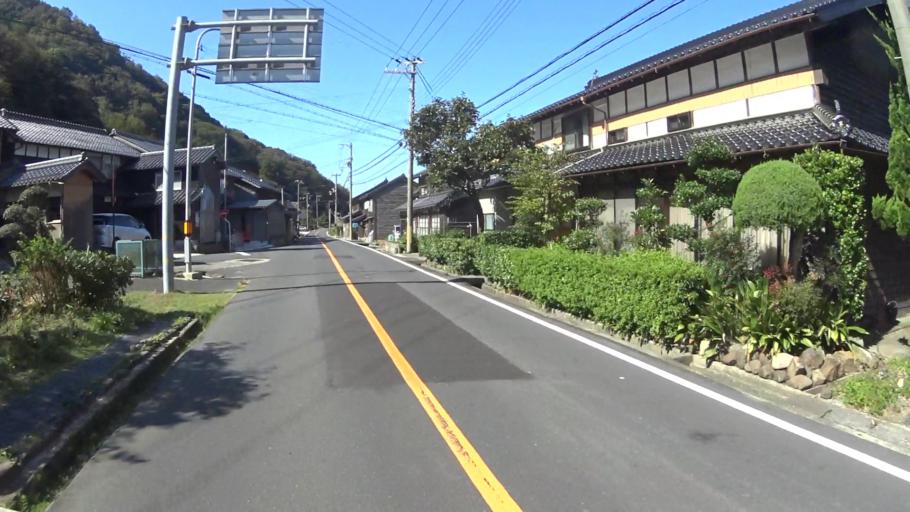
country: JP
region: Kyoto
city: Miyazu
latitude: 35.7473
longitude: 135.1636
